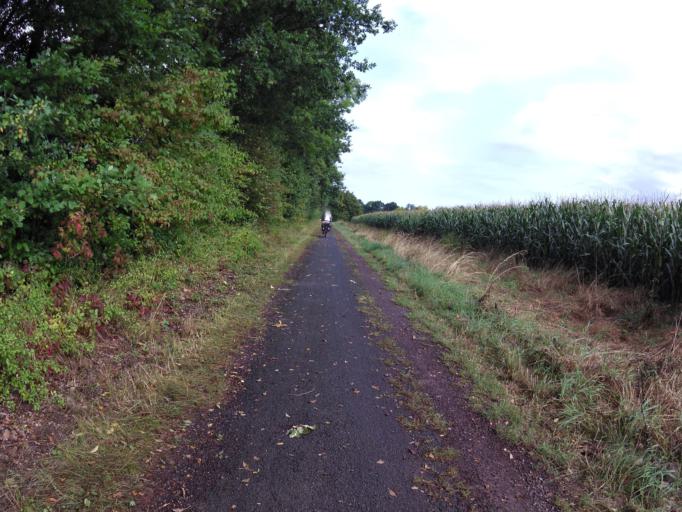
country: DE
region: Lower Saxony
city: Marklohe
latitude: 52.6652
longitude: 9.1731
